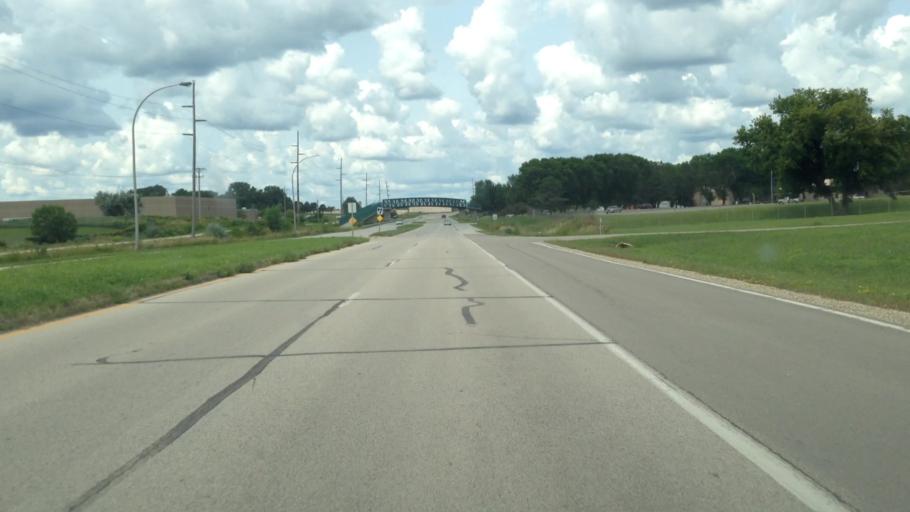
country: US
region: Minnesota
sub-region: Olmsted County
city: Rochester
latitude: 44.0497
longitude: -92.5091
